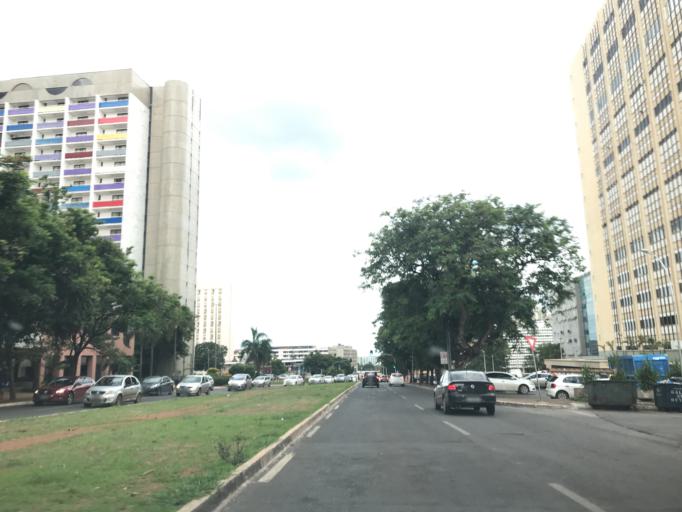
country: BR
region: Federal District
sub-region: Brasilia
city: Brasilia
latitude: -15.7959
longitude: -47.8897
